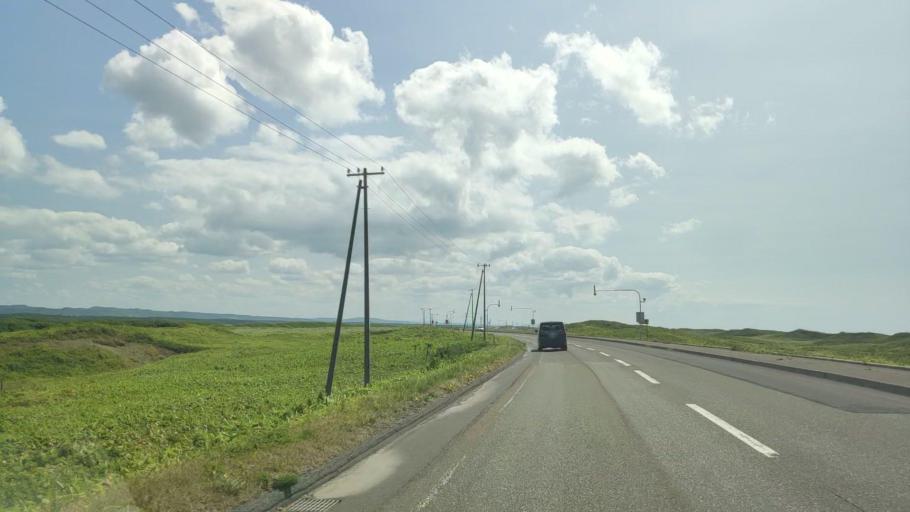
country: JP
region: Hokkaido
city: Makubetsu
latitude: 44.9496
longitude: 141.7101
